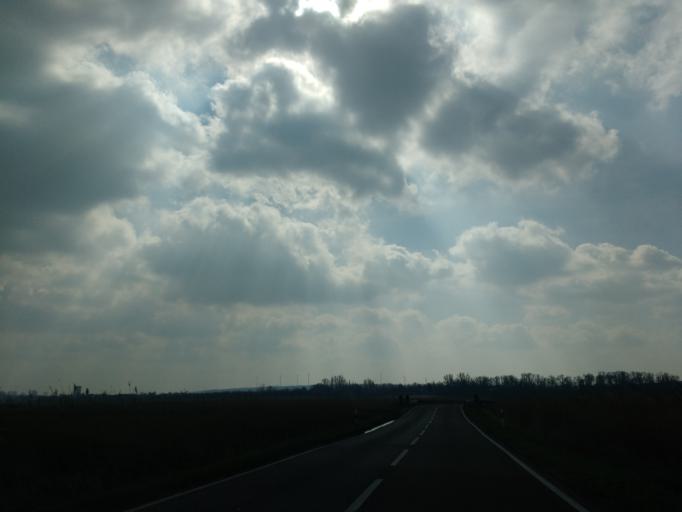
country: DE
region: Saxony-Anhalt
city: Roblingen am See
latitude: 51.4758
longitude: 11.6761
